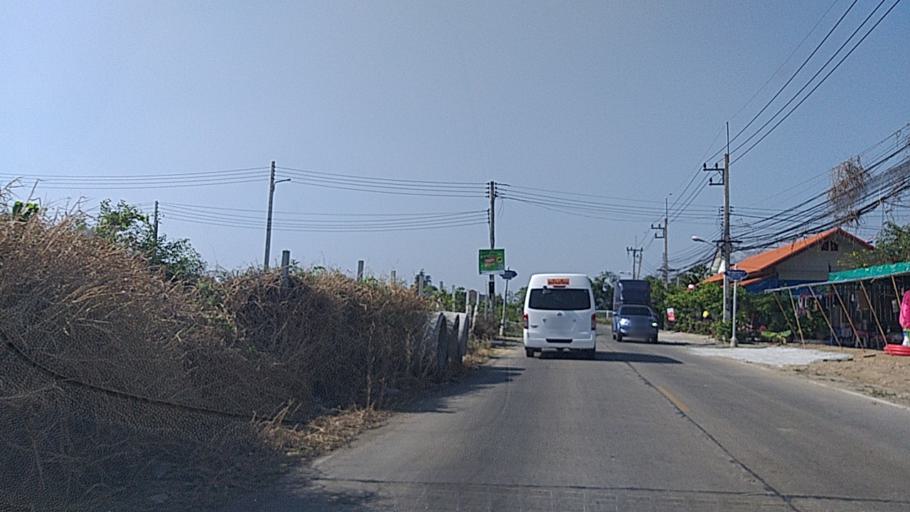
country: TH
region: Nakhon Pathom
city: Salaya
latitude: 13.8232
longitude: 100.3090
